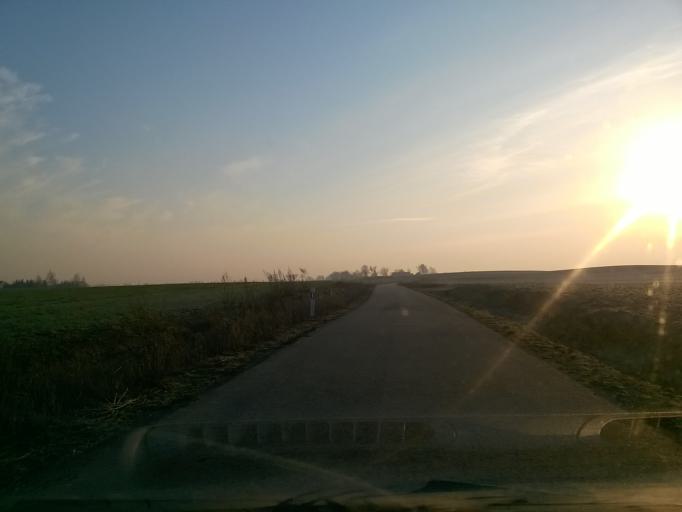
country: PL
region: Kujawsko-Pomorskie
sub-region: Powiat sepolenski
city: Sosno
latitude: 53.4504
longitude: 17.7167
